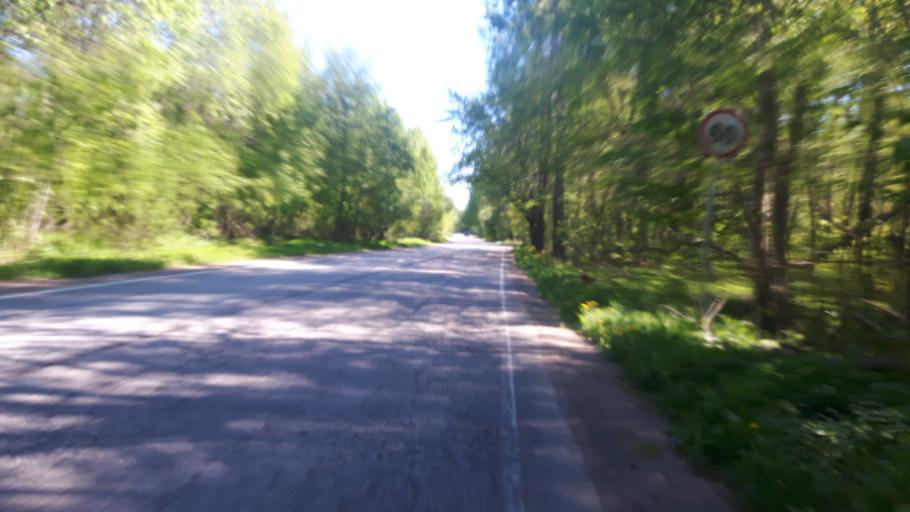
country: RU
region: Leningrad
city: Glebychevo
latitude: 60.2850
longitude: 28.8781
